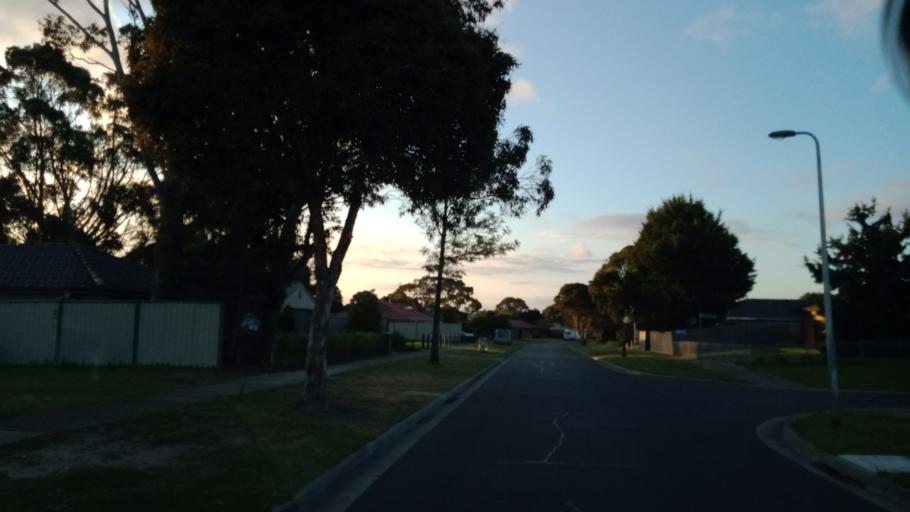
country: AU
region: Victoria
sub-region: Casey
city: Cranbourne North
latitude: -38.0789
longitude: 145.2716
